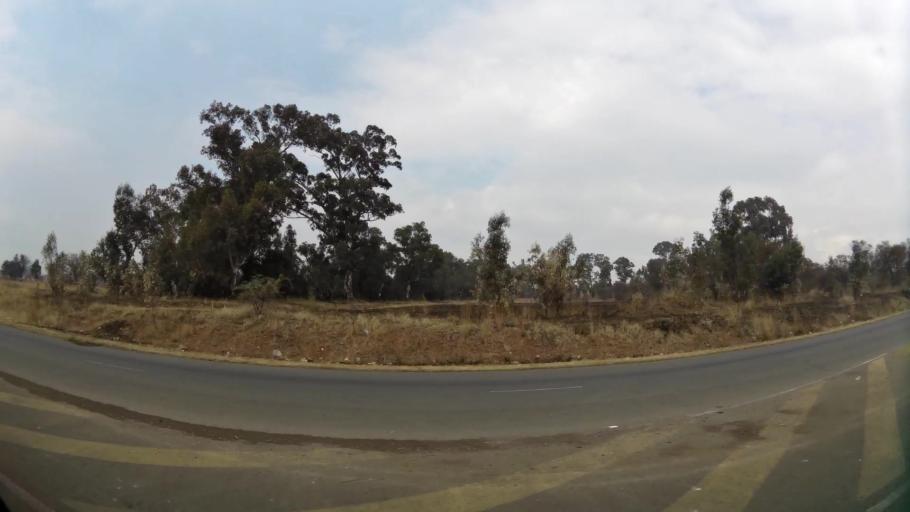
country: ZA
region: Gauteng
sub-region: Sedibeng District Municipality
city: Vanderbijlpark
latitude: -26.6740
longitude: 27.8391
